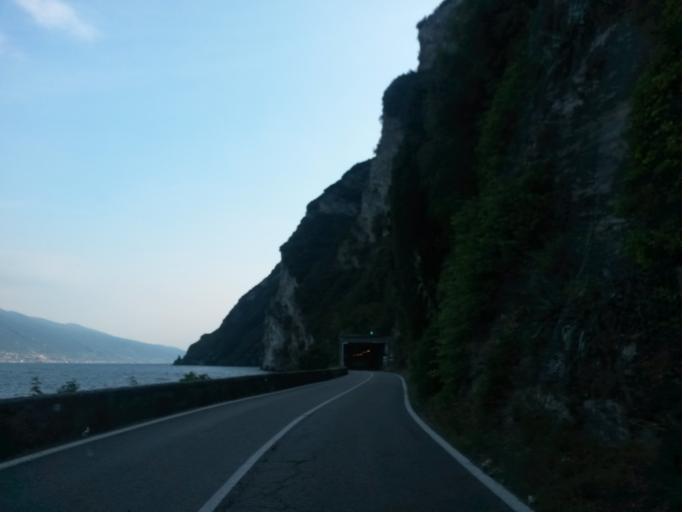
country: IT
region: Lombardy
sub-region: Provincia di Brescia
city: Limone sul Garda
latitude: 45.7947
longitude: 10.7821
